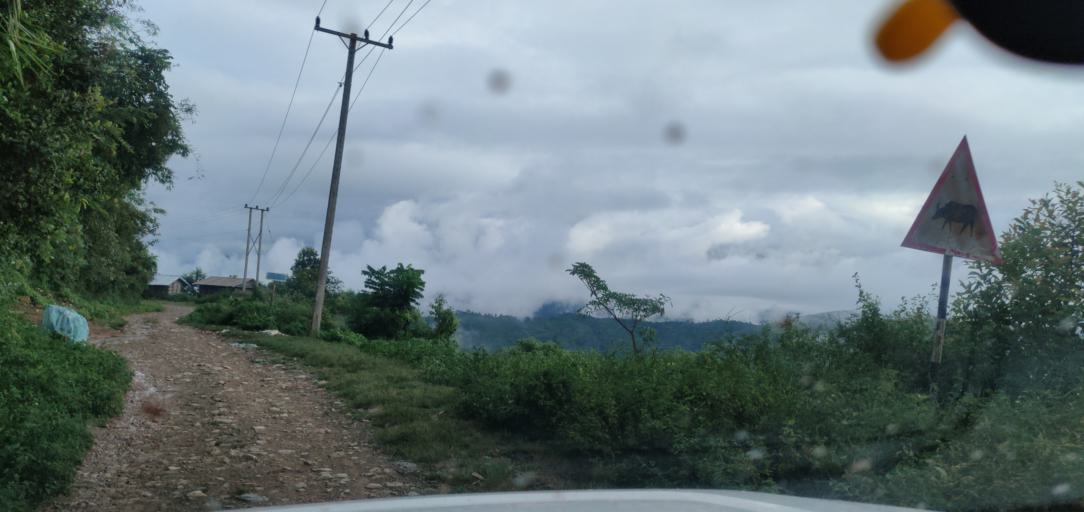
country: LA
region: Phongsali
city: Phongsali
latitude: 21.4421
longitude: 102.2940
